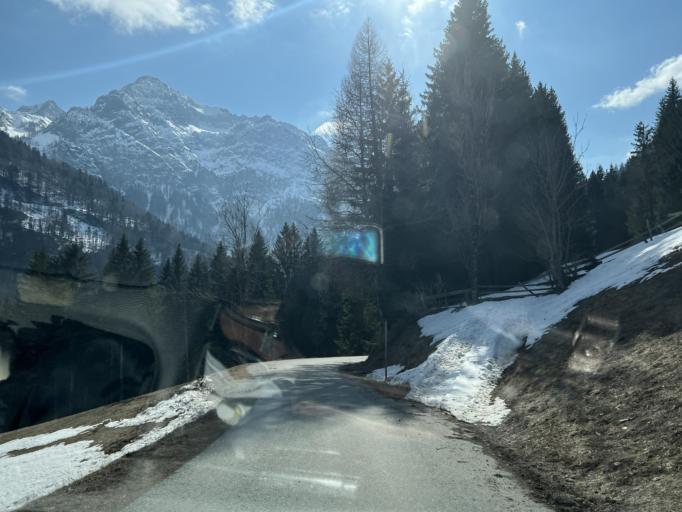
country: AT
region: Carinthia
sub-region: Politischer Bezirk Spittal an der Drau
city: Oberdrauburg
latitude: 46.6547
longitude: 12.9760
